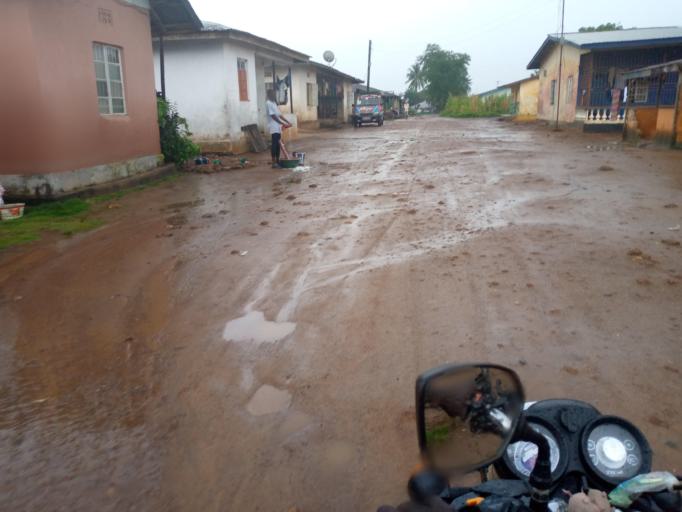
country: SL
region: Eastern Province
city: Kenema
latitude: 7.8844
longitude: -11.1811
